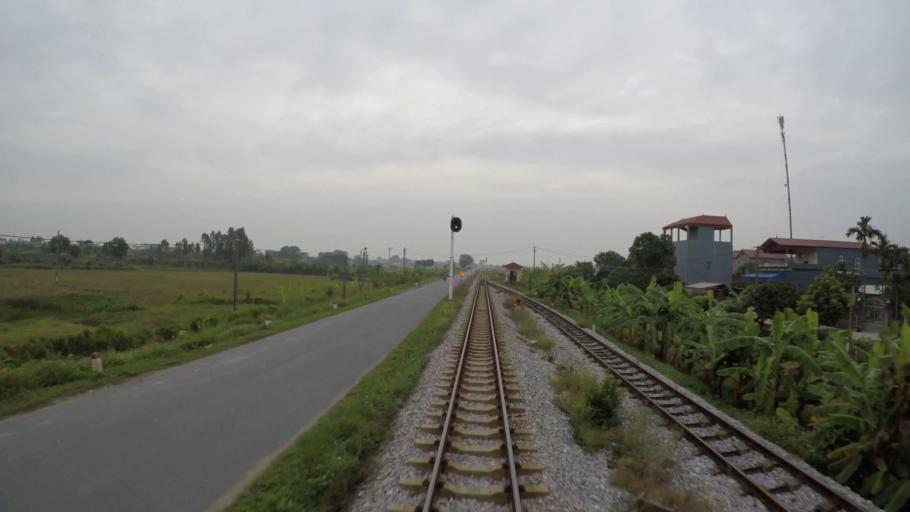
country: VN
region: Hung Yen
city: Ban Yen Nhan
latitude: 20.9722
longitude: 106.0973
